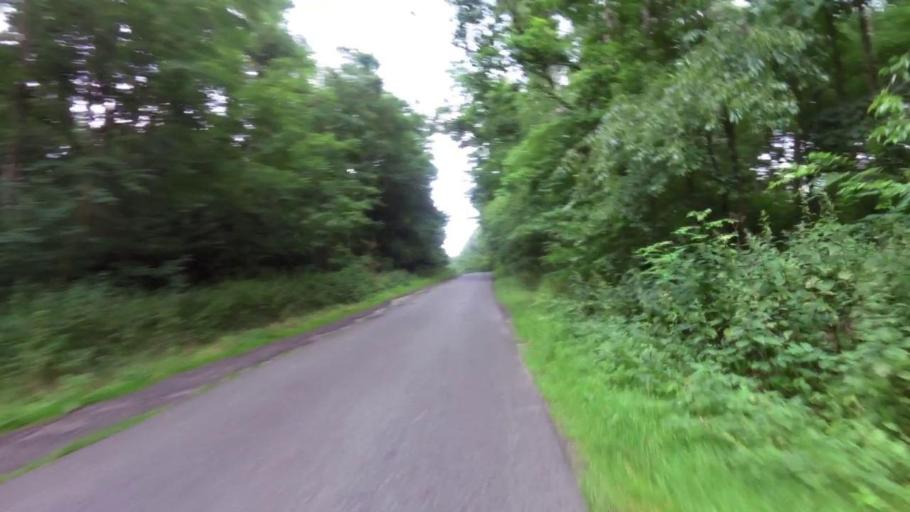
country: PL
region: West Pomeranian Voivodeship
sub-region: Powiat gryfinski
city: Chojna
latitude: 52.9100
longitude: 14.4705
